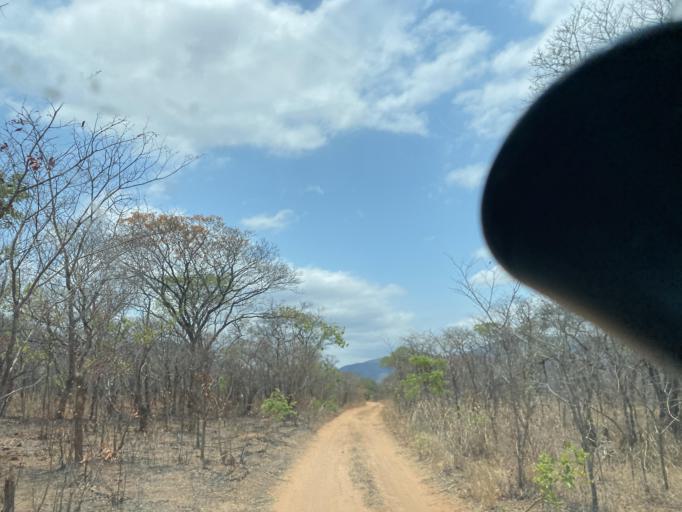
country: ZM
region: Lusaka
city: Luangwa
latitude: -15.1794
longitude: 29.7157
